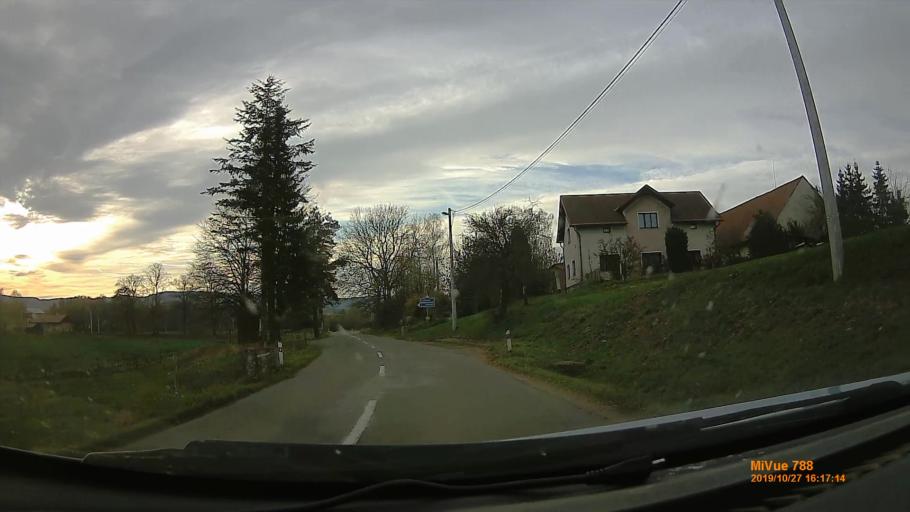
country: CZ
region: Kralovehradecky
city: Broumov
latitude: 50.5632
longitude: 16.3673
